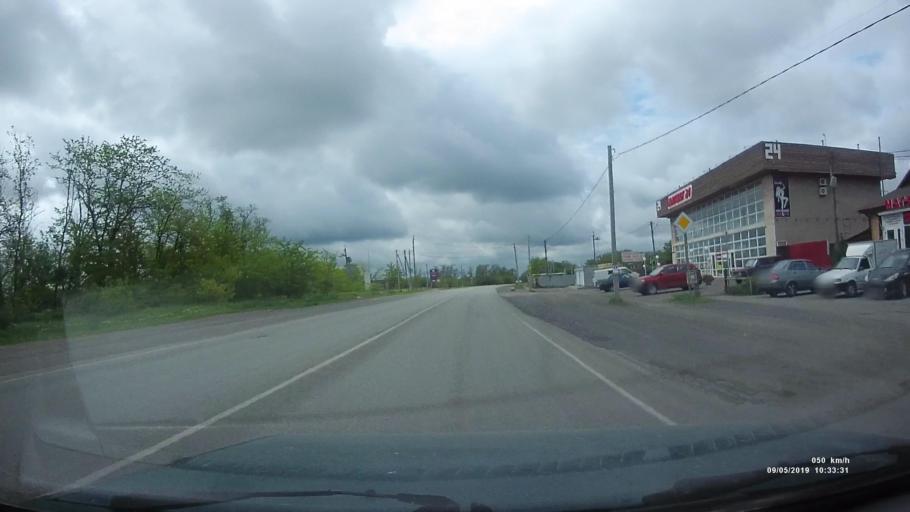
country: RU
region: Rostov
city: Azov
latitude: 47.0630
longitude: 39.4247
